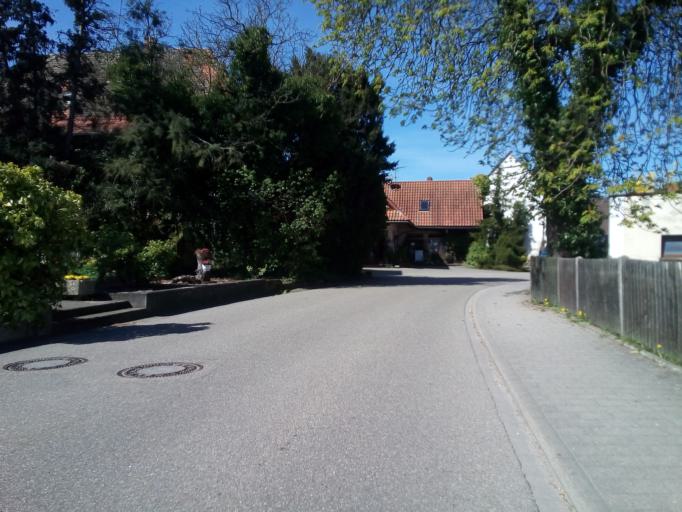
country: DE
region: Baden-Wuerttemberg
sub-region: Freiburg Region
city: Rheinau
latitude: 48.6497
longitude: 7.9277
